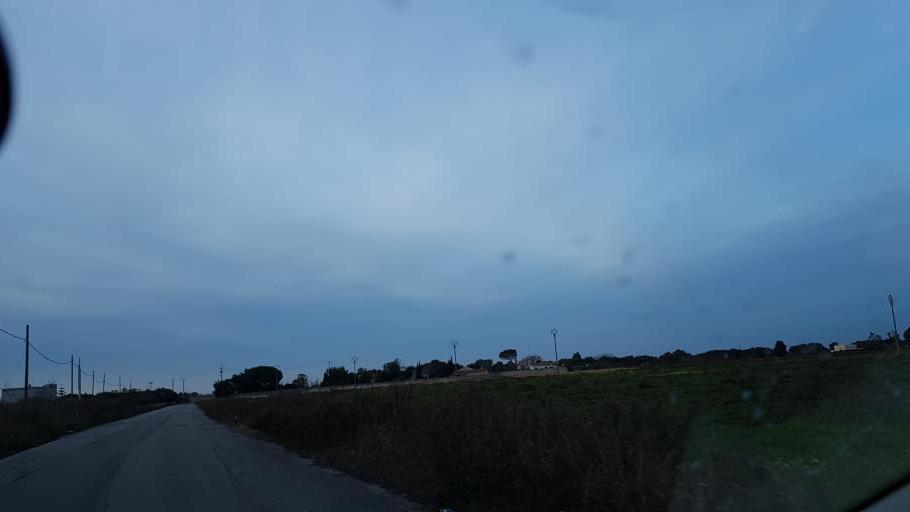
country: IT
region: Apulia
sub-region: Provincia di Brindisi
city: Brindisi
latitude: 40.6531
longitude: 17.9143
